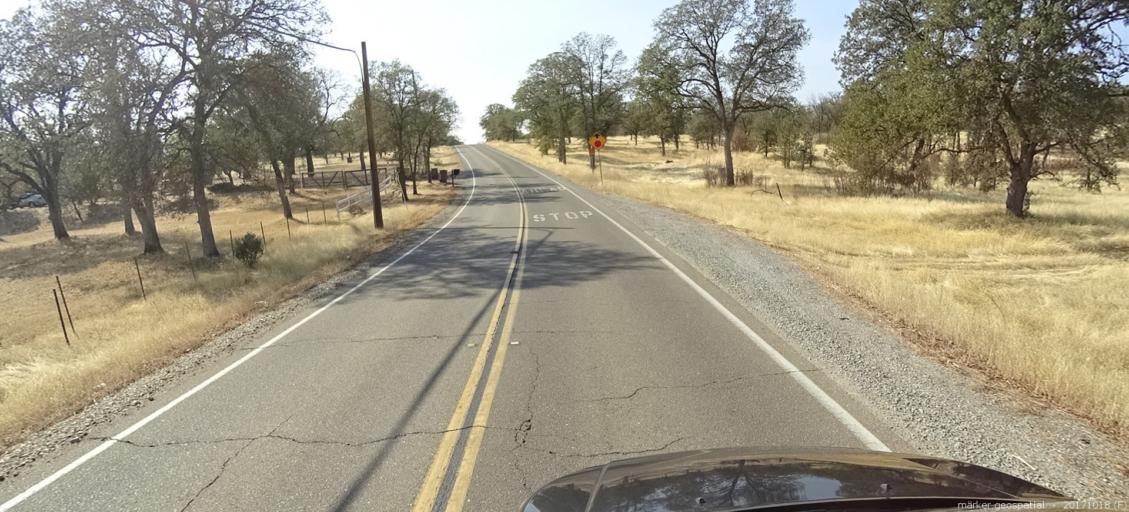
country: US
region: California
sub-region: Shasta County
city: Palo Cedro
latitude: 40.5640
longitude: -122.2742
